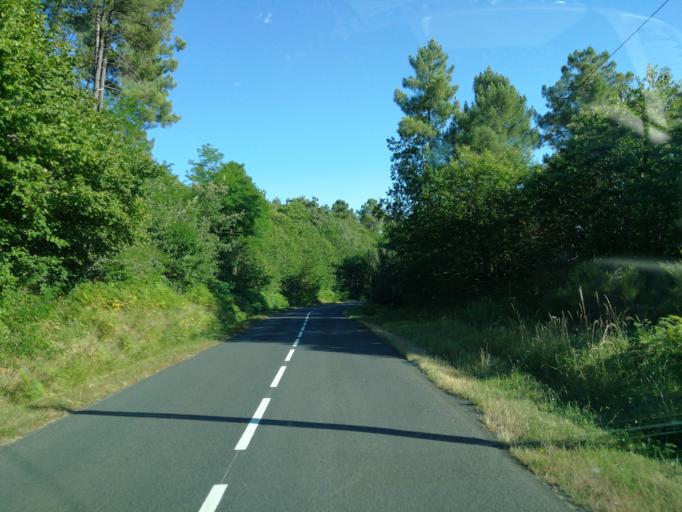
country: FR
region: Midi-Pyrenees
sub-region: Departement du Lot
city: Salviac
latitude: 44.6070
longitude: 1.2017
